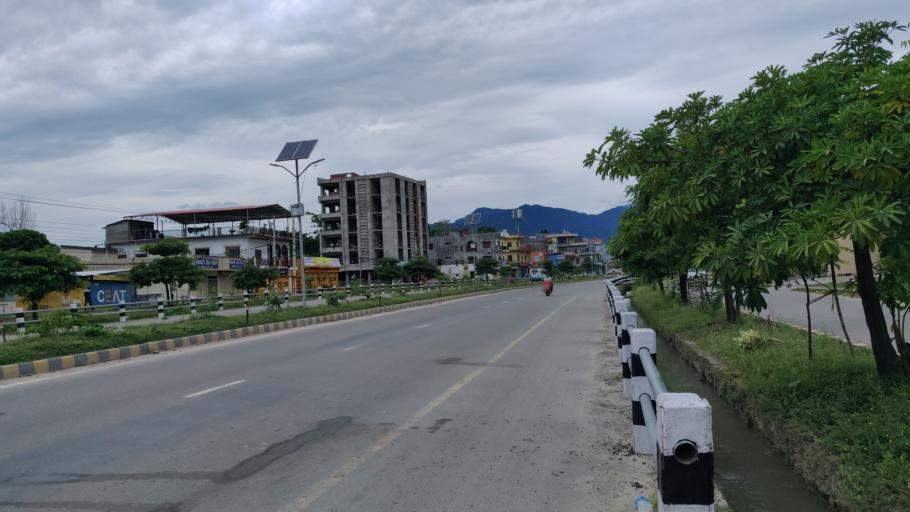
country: NP
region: Western Region
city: Butwal
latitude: 27.6628
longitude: 83.4654
